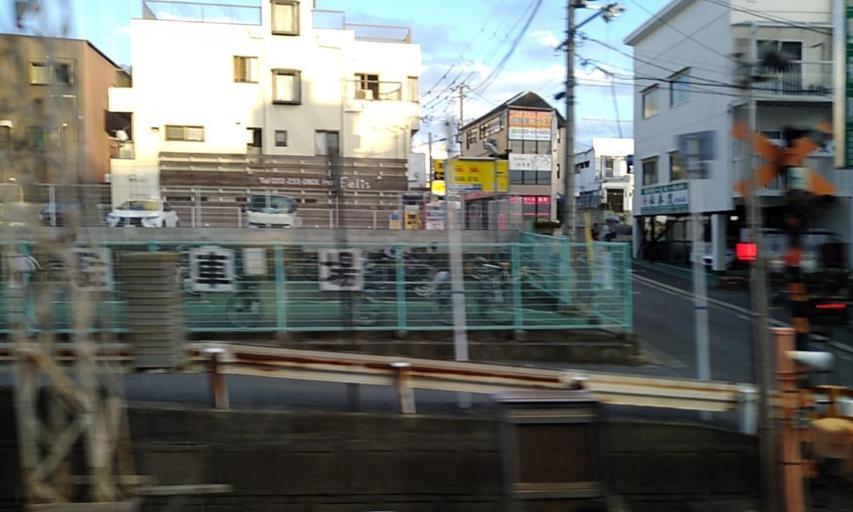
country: JP
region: Osaka
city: Sakai
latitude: 34.5733
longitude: 135.4843
